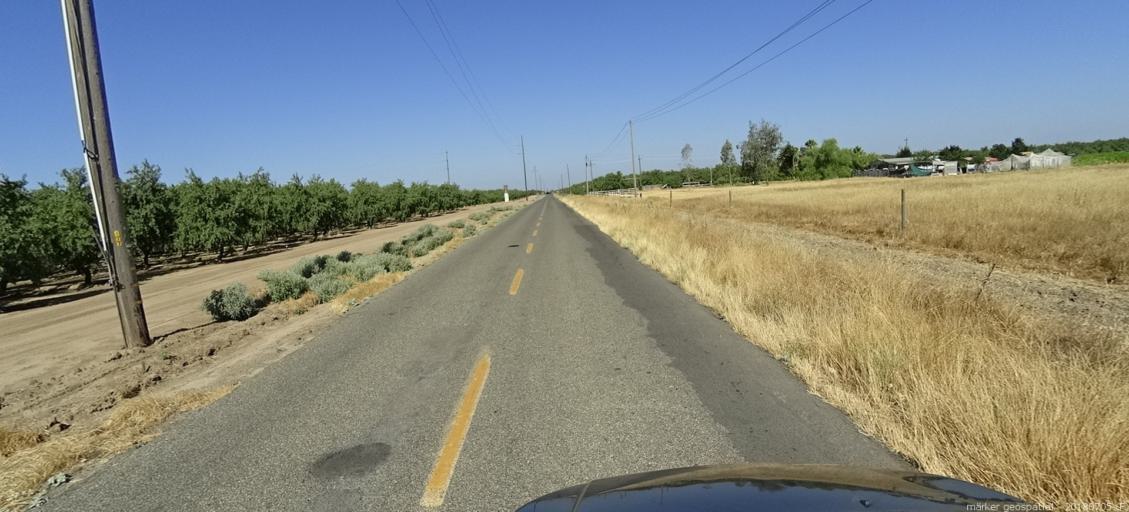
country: US
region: California
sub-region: Madera County
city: Fairmead
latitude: 37.1270
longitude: -120.1452
